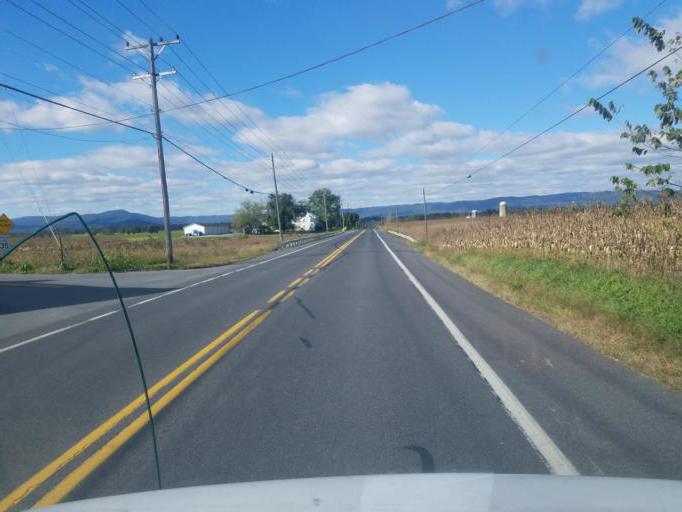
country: US
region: Pennsylvania
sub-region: Franklin County
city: Mercersburg
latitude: 39.8032
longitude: -77.8334
